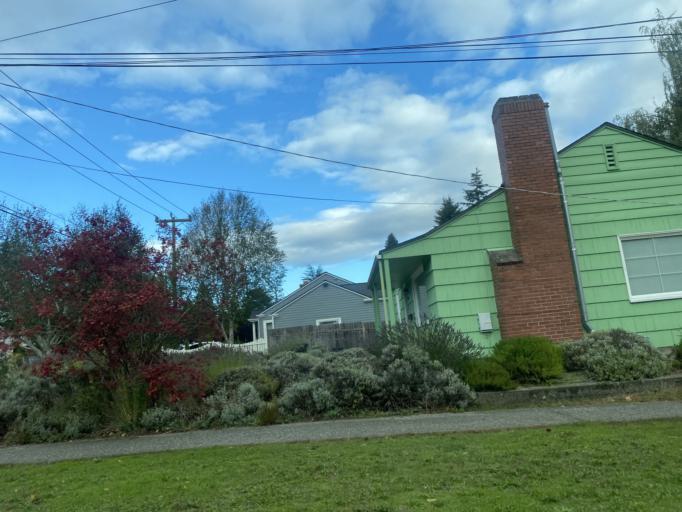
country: US
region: Washington
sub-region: King County
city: Seattle
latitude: 47.6450
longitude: -122.4021
